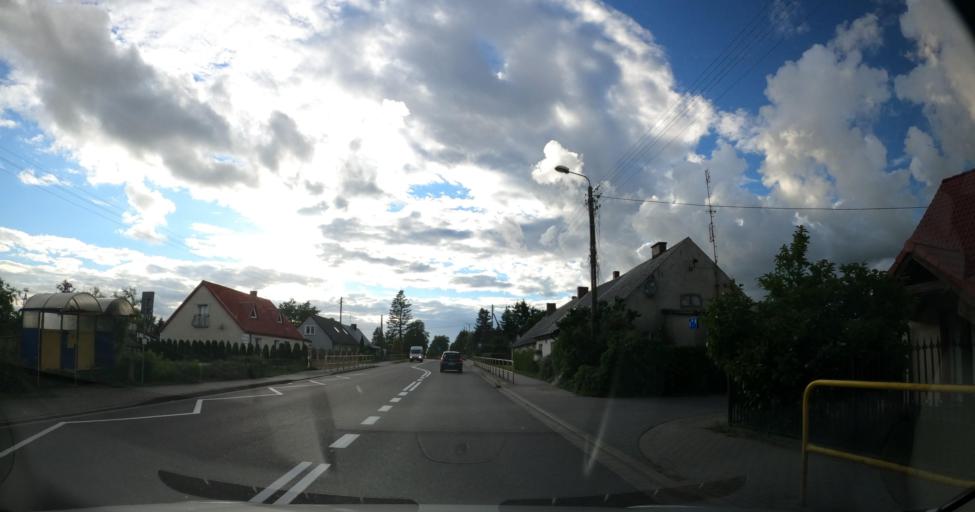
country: PL
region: Pomeranian Voivodeship
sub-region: Powiat slupski
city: Potegowo
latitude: 54.4225
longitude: 17.3797
